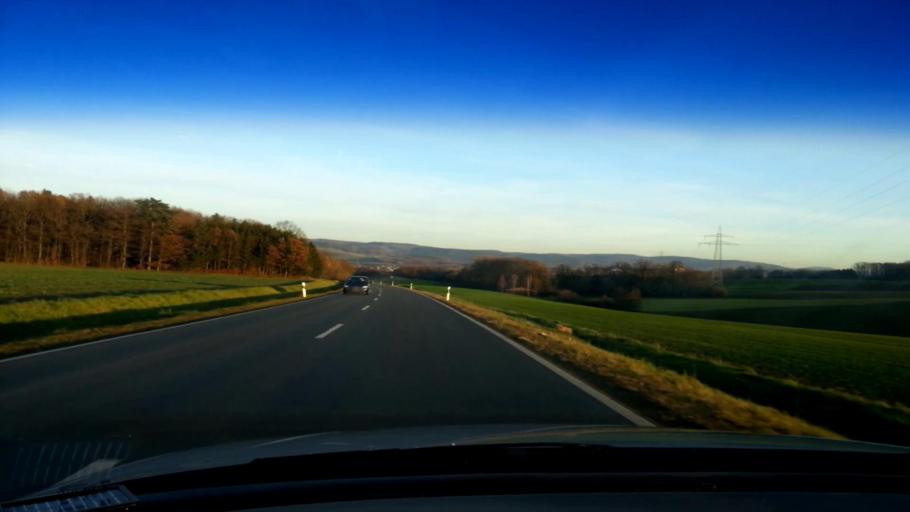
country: DE
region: Bavaria
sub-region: Upper Franconia
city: Ebensfeld
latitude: 50.0661
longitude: 10.9225
